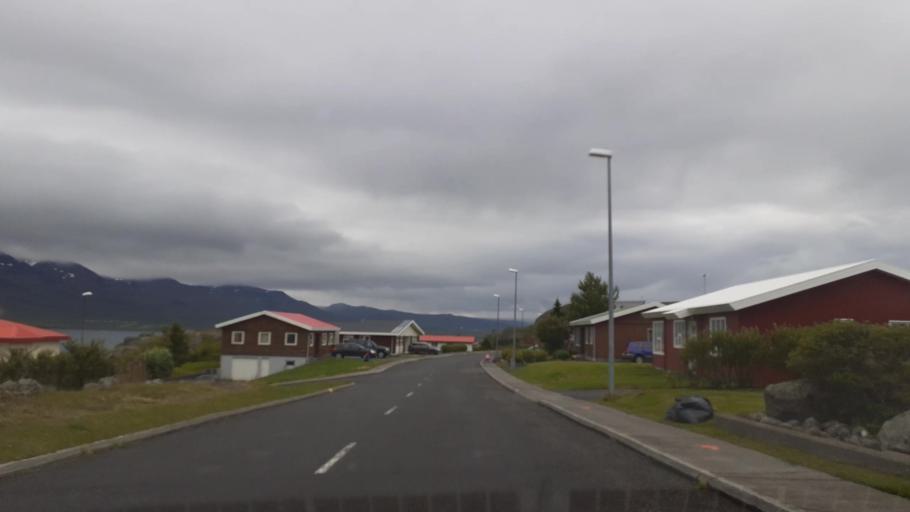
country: IS
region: East
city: Egilsstadir
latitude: 65.7537
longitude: -14.8330
